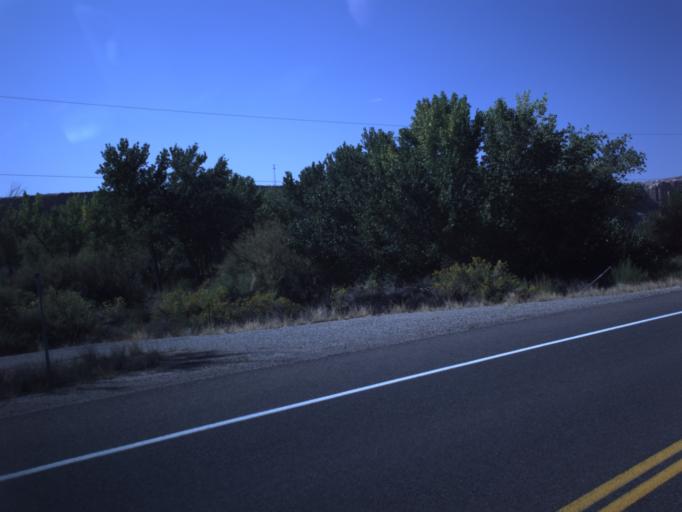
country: US
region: Utah
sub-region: San Juan County
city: Blanding
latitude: 37.2833
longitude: -109.5496
